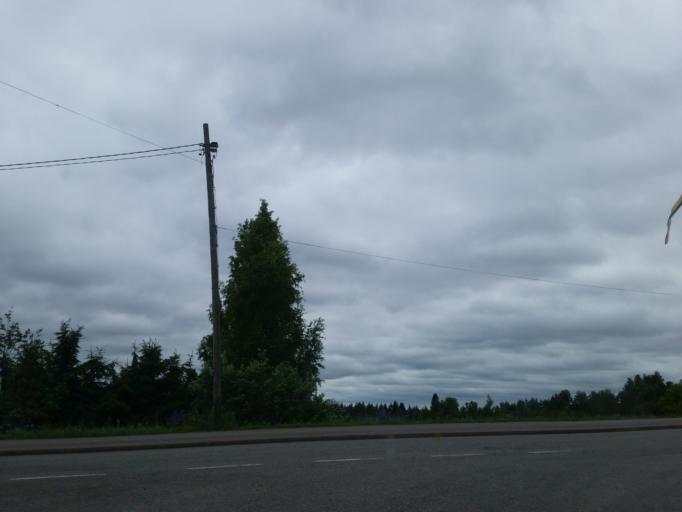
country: FI
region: Northern Savo
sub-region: Koillis-Savo
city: Kaavi
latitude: 62.9748
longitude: 28.4930
